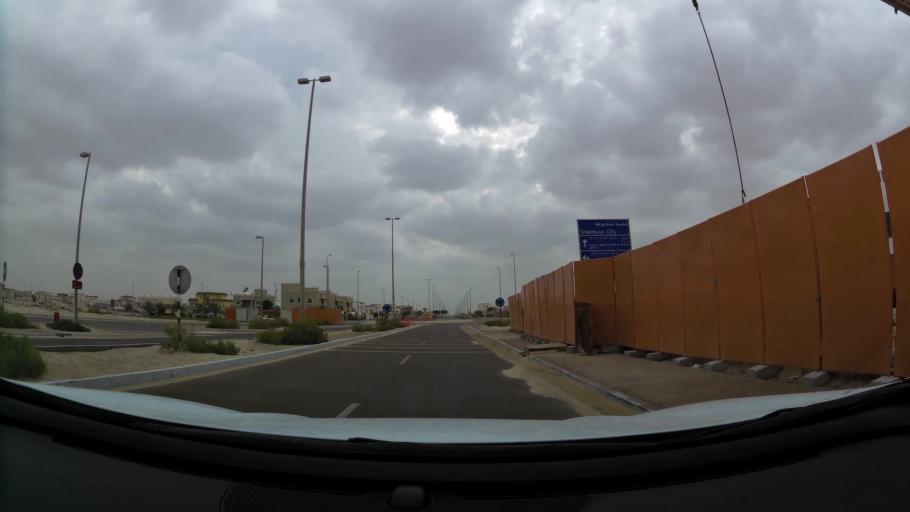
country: AE
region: Abu Dhabi
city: Abu Dhabi
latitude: 24.3709
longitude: 54.6399
